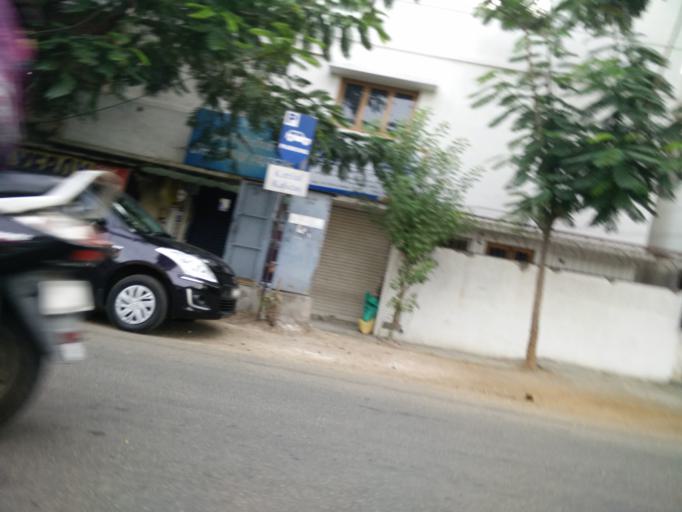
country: IN
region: Tamil Nadu
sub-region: Coimbatore
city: Coimbatore
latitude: 11.0257
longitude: 76.9417
